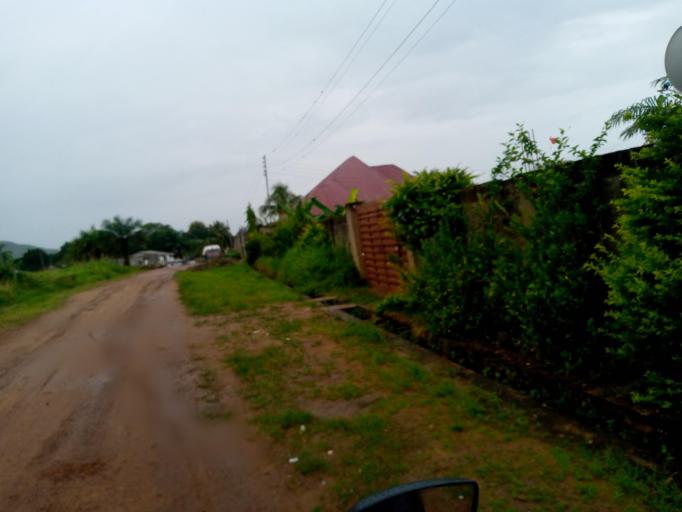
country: SL
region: Eastern Province
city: Kenema
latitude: 7.8448
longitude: -11.2045
